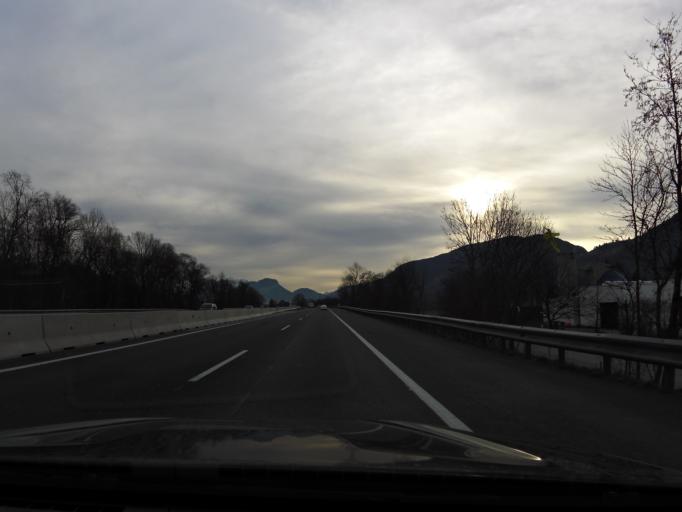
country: AT
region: Tyrol
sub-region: Politischer Bezirk Kufstein
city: Radfeld
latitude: 47.4597
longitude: 11.9301
